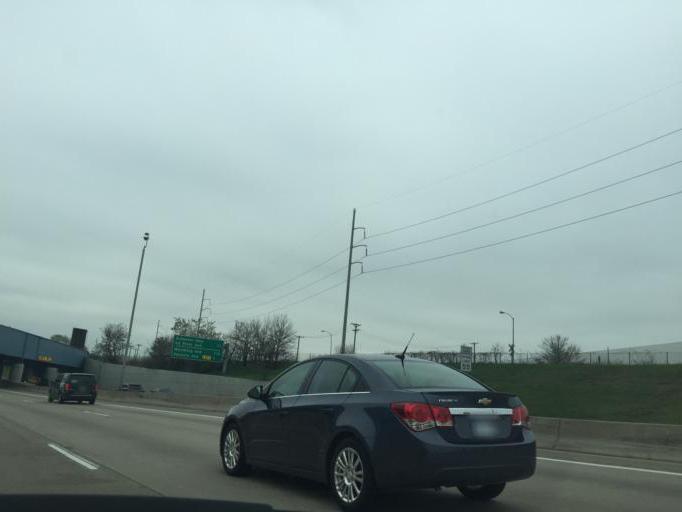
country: US
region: Michigan
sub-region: Wayne County
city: Dearborn
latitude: 42.3796
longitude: -83.1908
